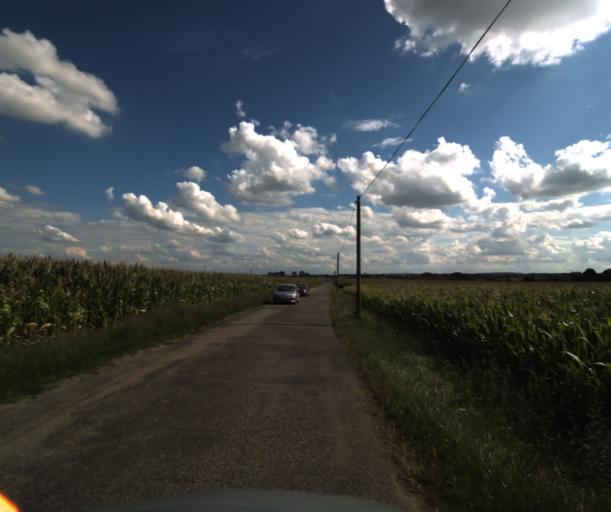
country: FR
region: Midi-Pyrenees
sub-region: Departement de la Haute-Garonne
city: Roquettes
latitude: 43.4849
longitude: 1.3692
